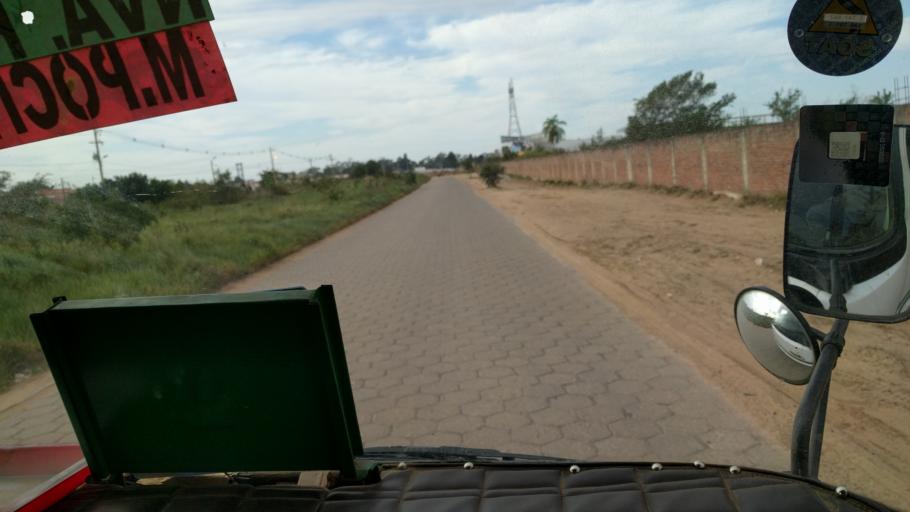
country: BO
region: Santa Cruz
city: Santa Cruz de la Sierra
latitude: -17.6924
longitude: -63.1441
